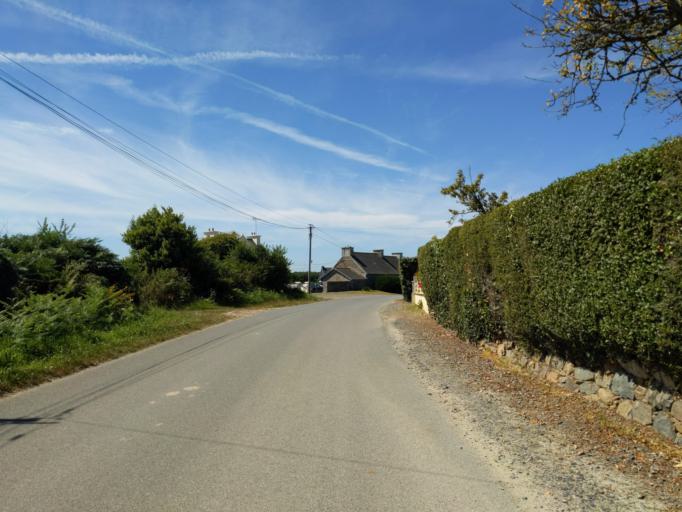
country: FR
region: Brittany
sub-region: Departement des Cotes-d'Armor
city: Pleumeur-Gautier
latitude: 48.8302
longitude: -3.1740
